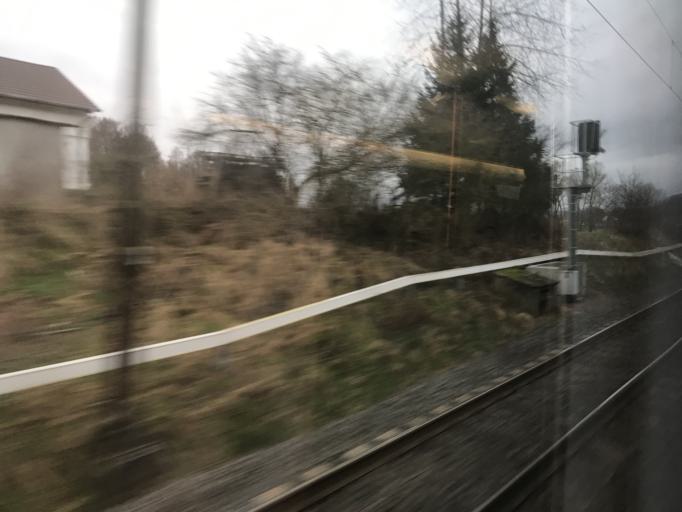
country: DE
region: Hesse
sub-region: Regierungsbezirk Kassel
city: Bad Hersfeld
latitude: 50.8187
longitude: 9.7296
